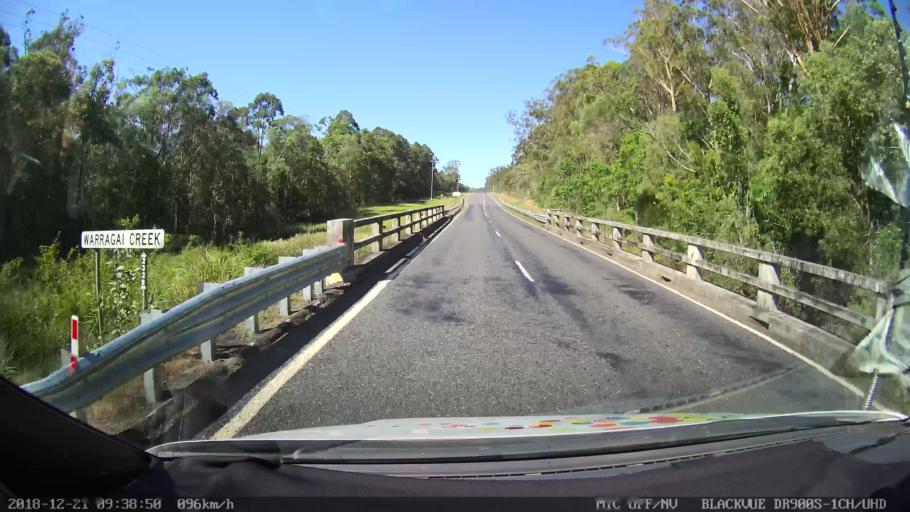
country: AU
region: New South Wales
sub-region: Clarence Valley
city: Grafton
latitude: -29.5544
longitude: 152.9792
